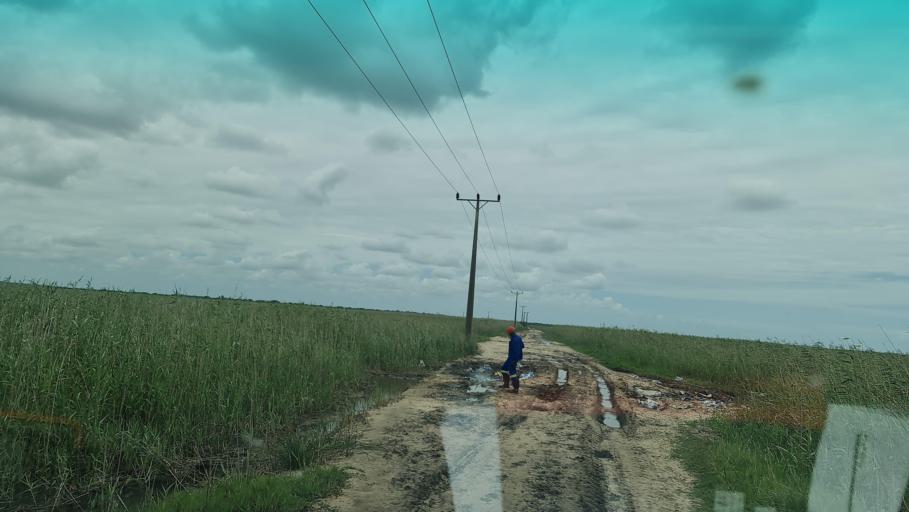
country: MZ
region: Maputo City
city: Maputo
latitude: -25.7185
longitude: 32.7006
